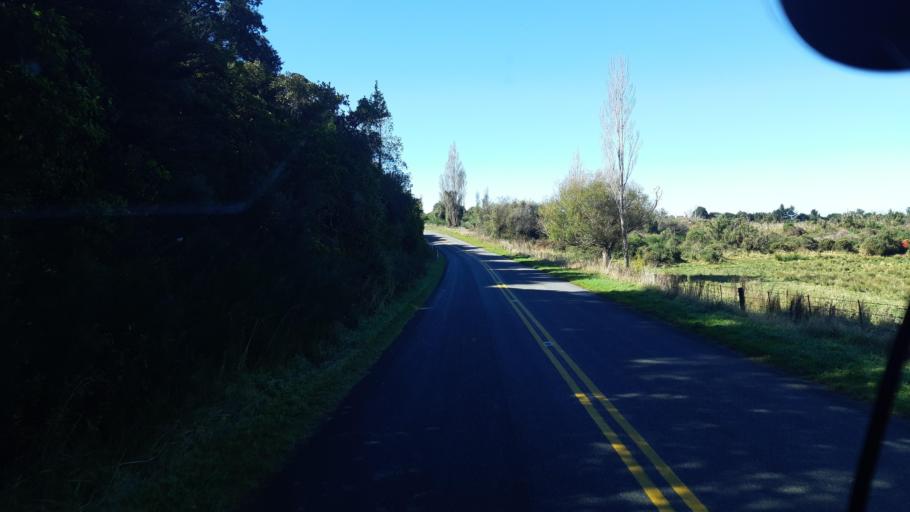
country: NZ
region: Canterbury
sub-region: Waimakariri District
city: Oxford
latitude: -43.2277
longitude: 172.2367
